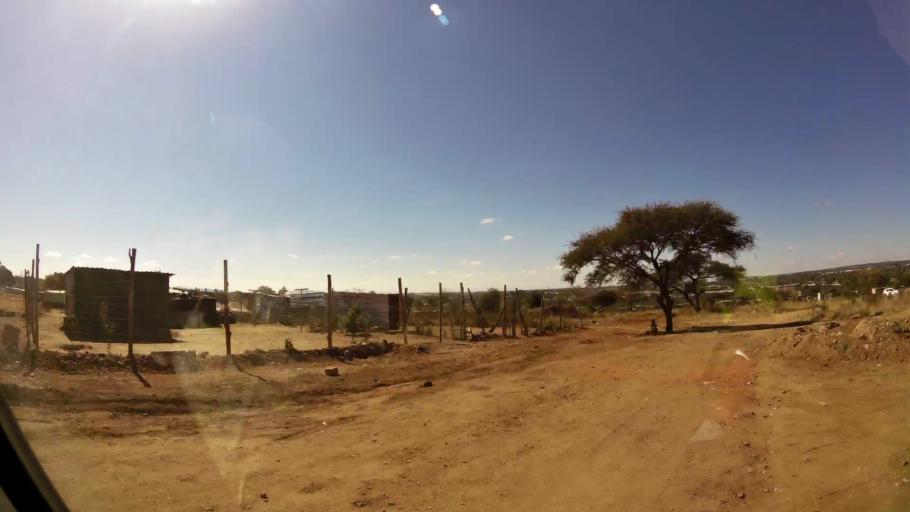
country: ZA
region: Limpopo
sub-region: Capricorn District Municipality
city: Polokwane
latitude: -23.8789
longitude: 29.4251
